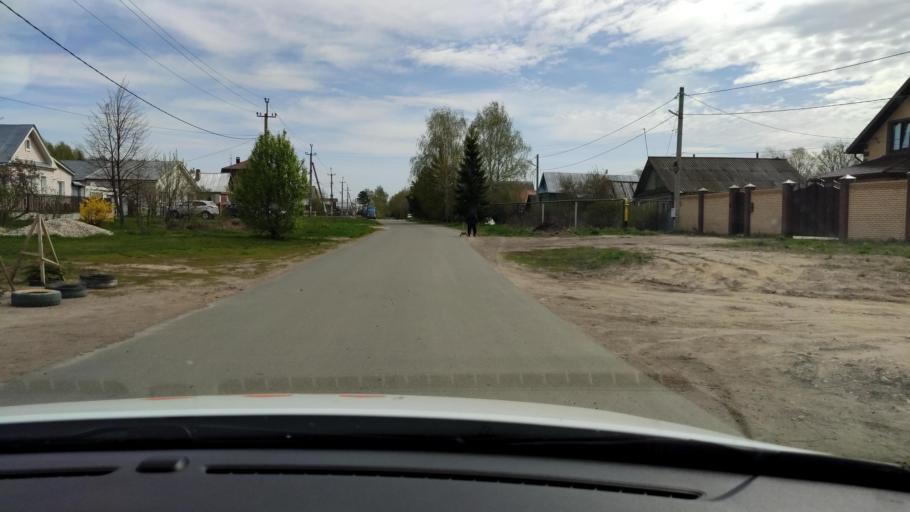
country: RU
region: Tatarstan
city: Osinovo
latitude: 55.8072
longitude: 48.8870
